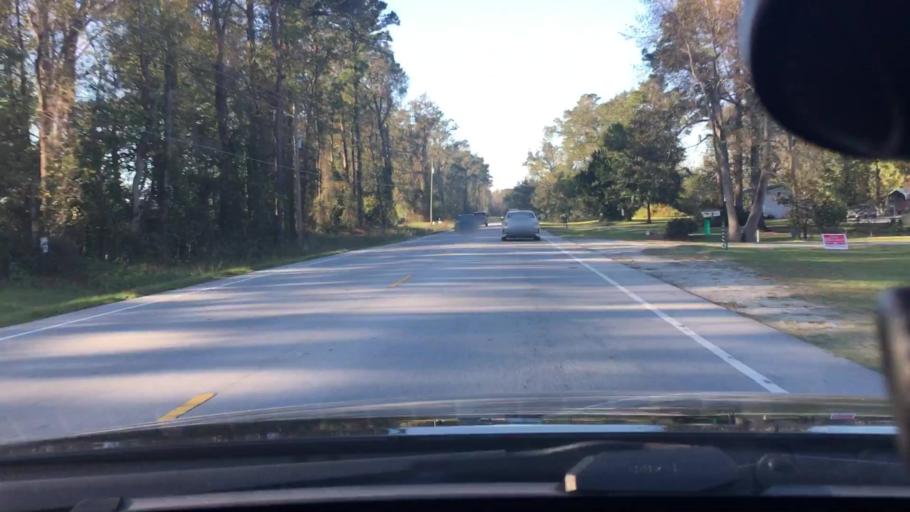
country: US
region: North Carolina
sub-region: Craven County
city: New Bern
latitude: 35.2228
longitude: -77.0679
